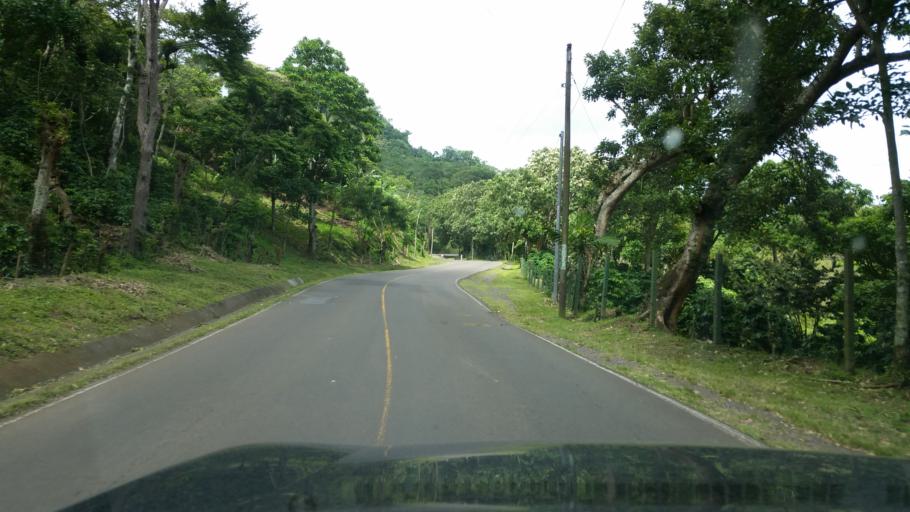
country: NI
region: Matagalpa
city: San Ramon
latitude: 12.9623
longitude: -85.8671
